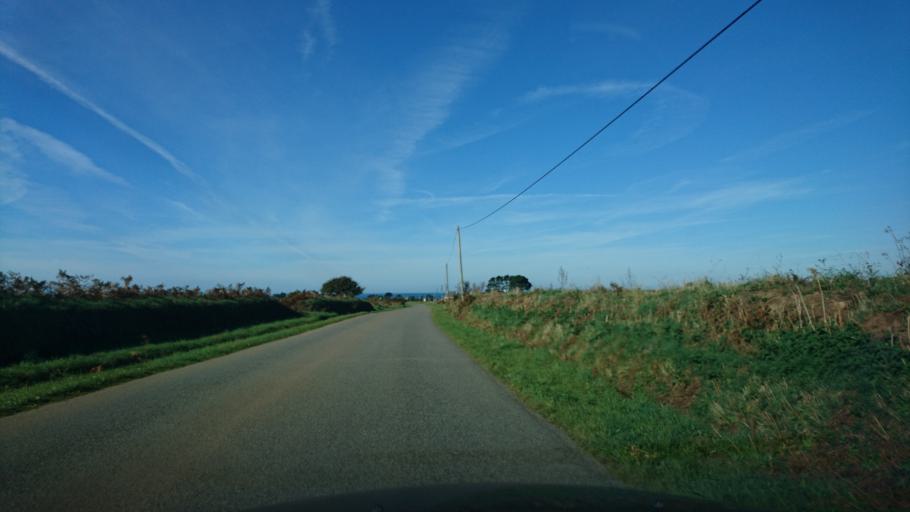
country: FR
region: Brittany
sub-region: Departement du Finistere
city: Lampaul-Plouarzel
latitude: 48.4281
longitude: -4.7538
